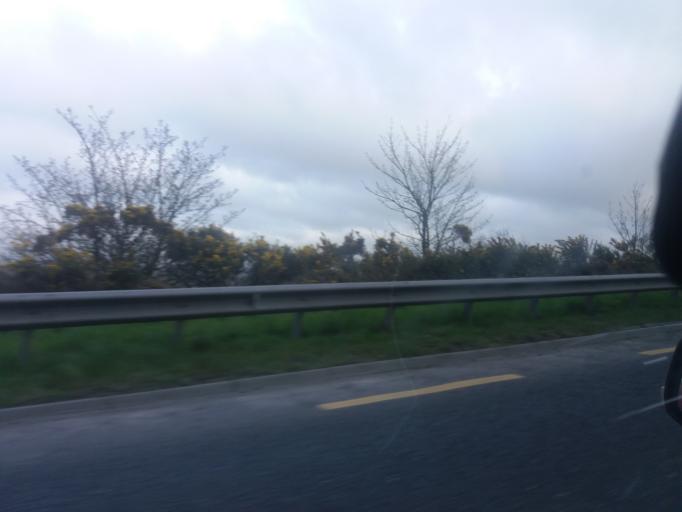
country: IE
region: Munster
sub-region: County Limerick
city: Newcastle West
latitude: 52.4252
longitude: -9.1282
